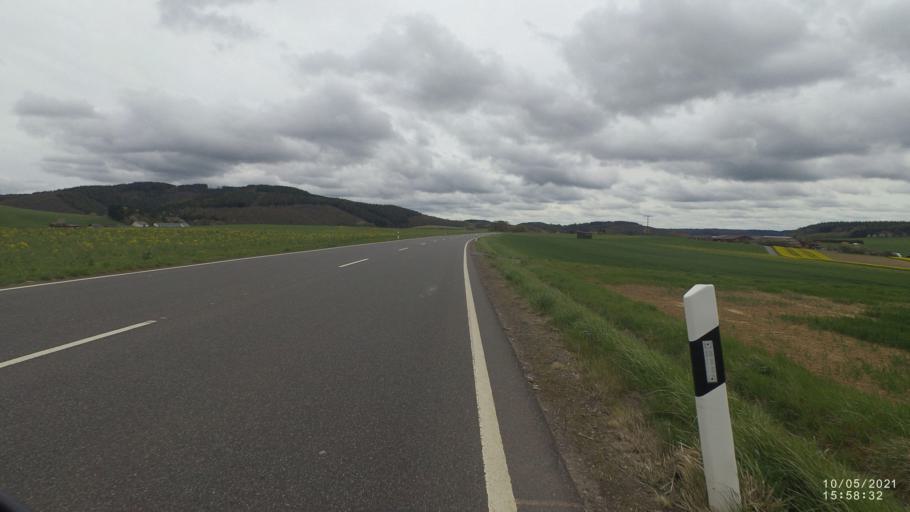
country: DE
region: Rheinland-Pfalz
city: Drees
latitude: 50.3570
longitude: 7.0084
